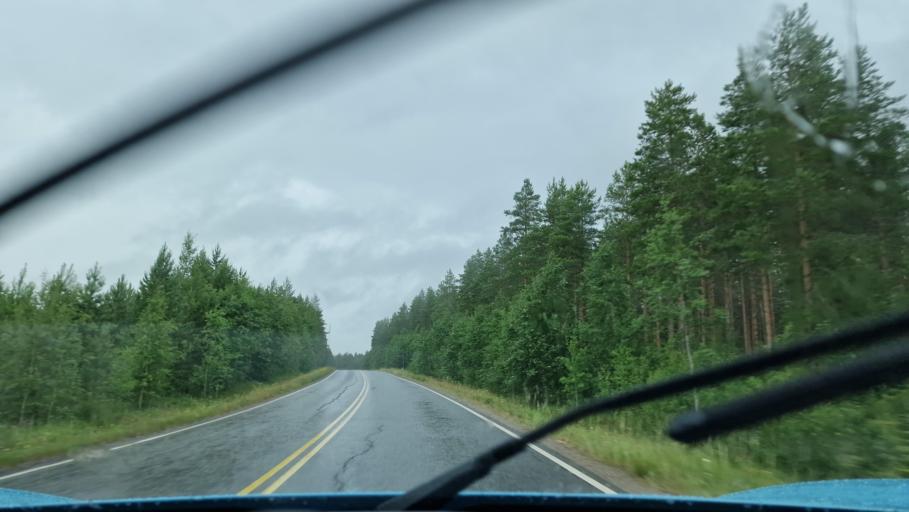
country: FI
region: Southern Ostrobothnia
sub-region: Jaerviseutu
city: Soini
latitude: 62.8123
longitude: 24.3597
